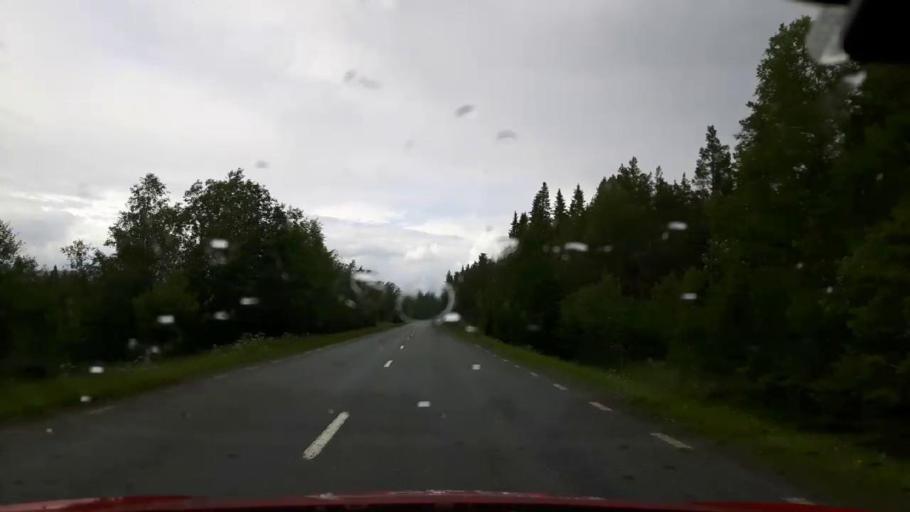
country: SE
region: Jaemtland
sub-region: Krokoms Kommun
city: Krokom
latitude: 63.4425
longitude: 14.1978
